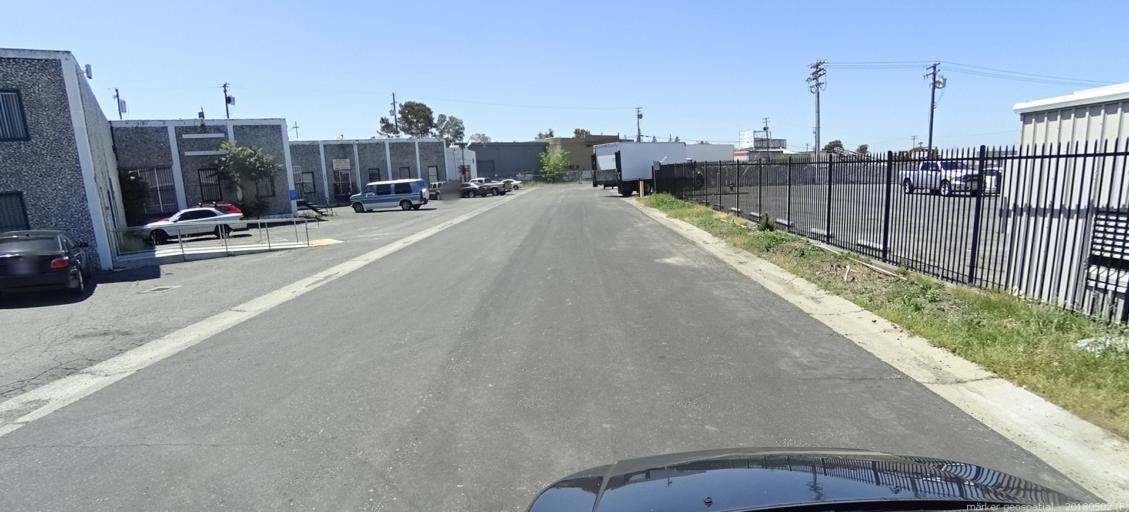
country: US
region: California
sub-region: Sacramento County
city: Sacramento
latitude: 38.6019
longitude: -121.4430
